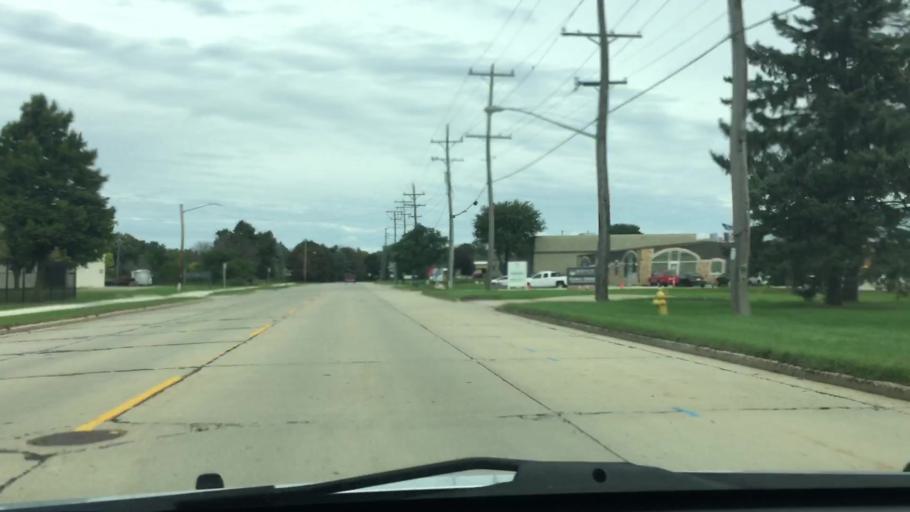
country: US
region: Wisconsin
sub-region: Waukesha County
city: Waukesha
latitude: 42.9993
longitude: -88.2489
